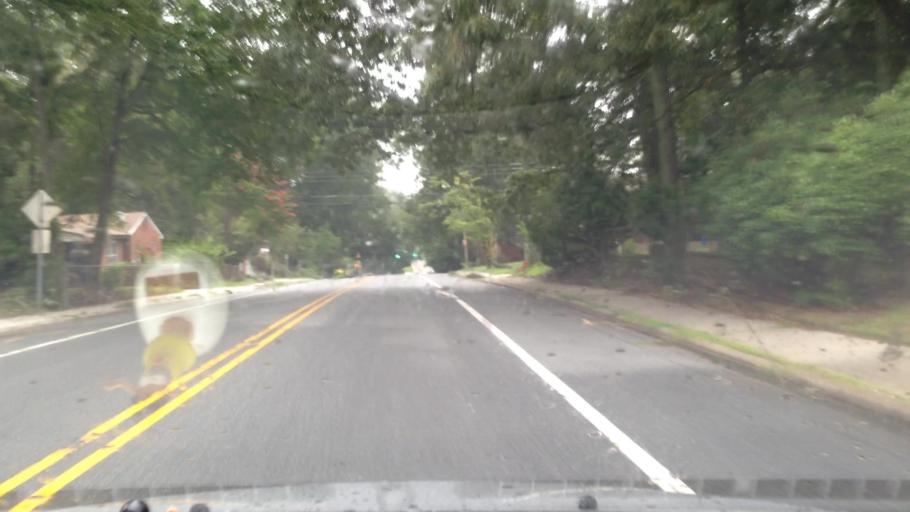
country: US
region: North Carolina
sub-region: Guilford County
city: Greensboro
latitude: 36.0540
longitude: -79.7643
